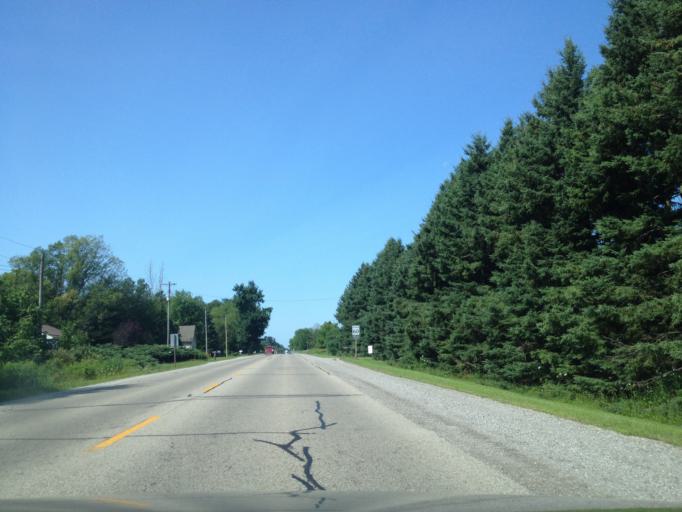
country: CA
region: Ontario
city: Norfolk County
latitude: 42.8029
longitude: -80.3991
